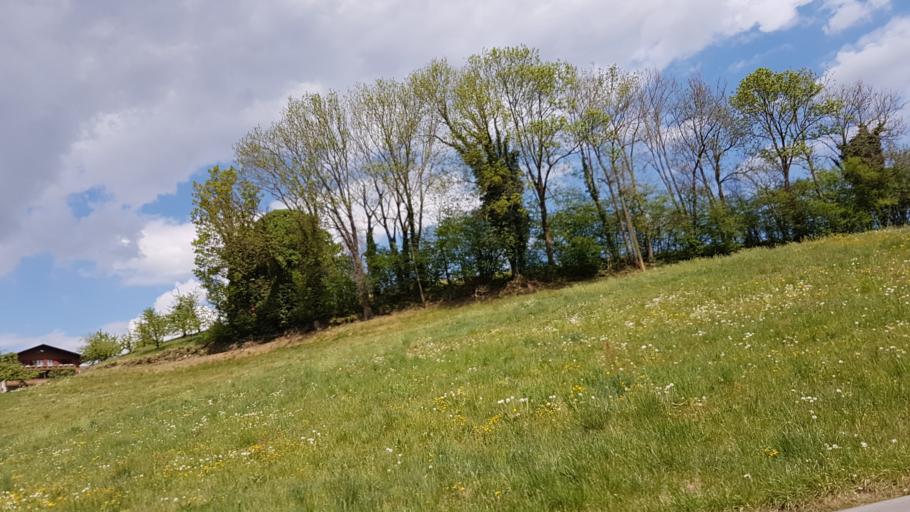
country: CH
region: Bern
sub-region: Thun District
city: Blumenstein
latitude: 46.7561
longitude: 7.5262
